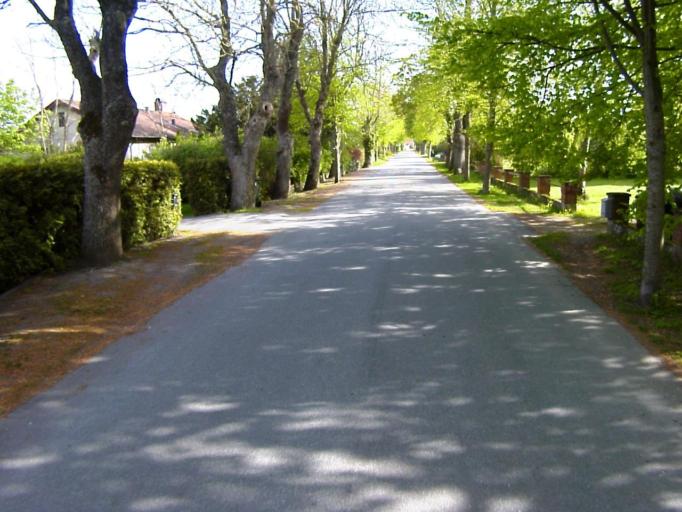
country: SE
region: Skane
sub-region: Kristianstads Kommun
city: Fjalkinge
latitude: 56.0395
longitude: 14.2782
